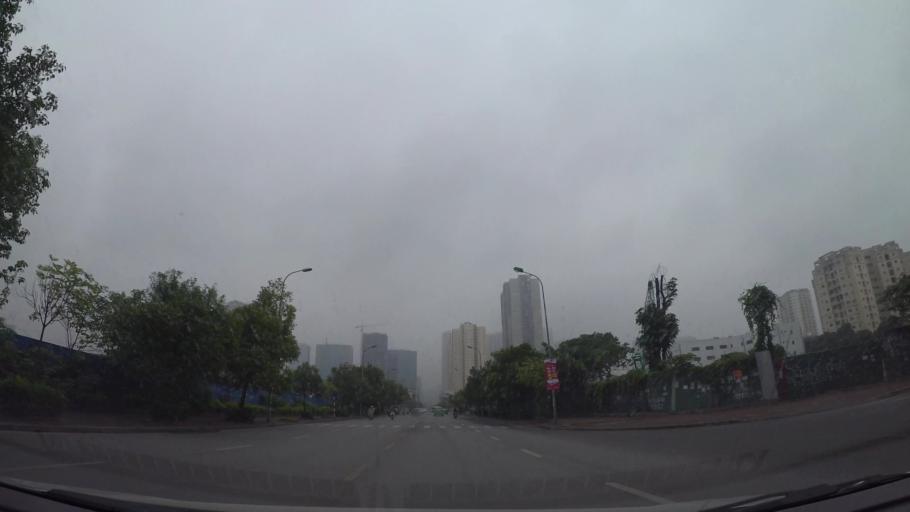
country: VN
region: Ha Noi
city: Thanh Xuan
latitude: 21.0130
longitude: 105.7915
